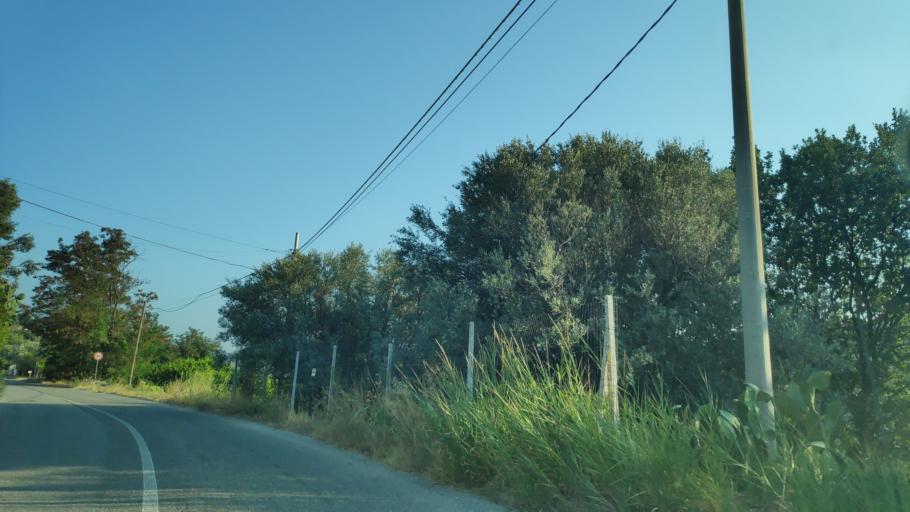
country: IT
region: Calabria
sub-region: Provincia di Reggio Calabria
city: Caulonia
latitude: 38.3877
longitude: 16.4325
